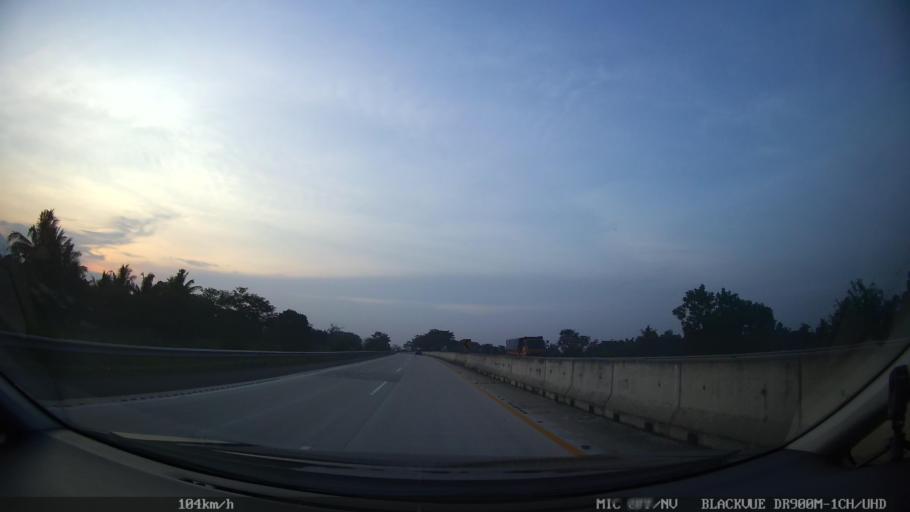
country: ID
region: Lampung
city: Penengahan
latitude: -5.7506
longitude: 105.7065
